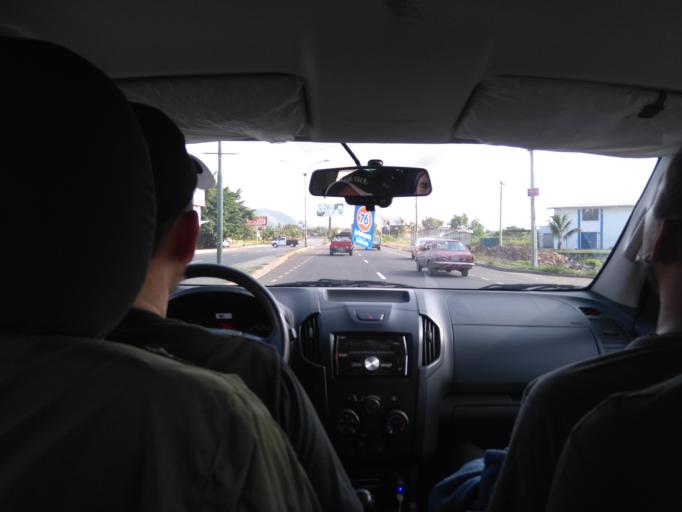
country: EC
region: Manabi
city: Portoviejo
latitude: -0.9990
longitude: -80.4664
